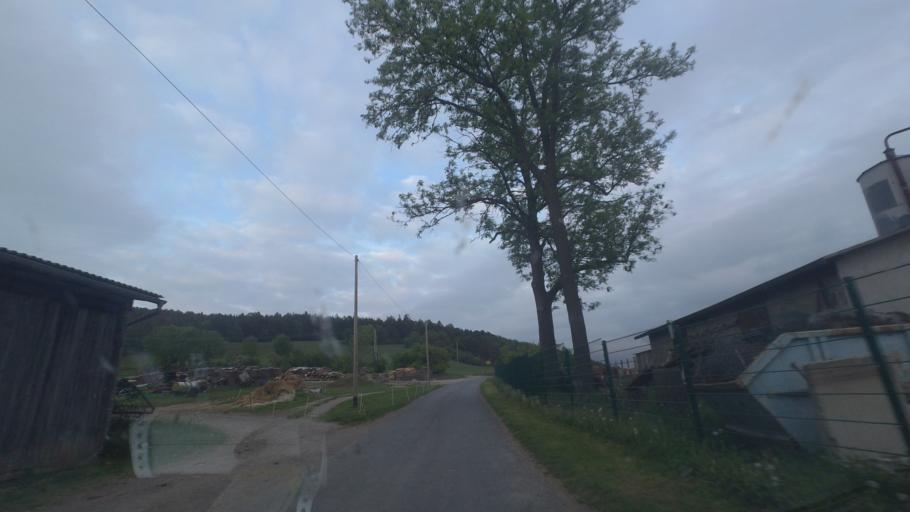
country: DE
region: Thuringia
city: Stadtilm
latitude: 50.7288
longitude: 11.0850
